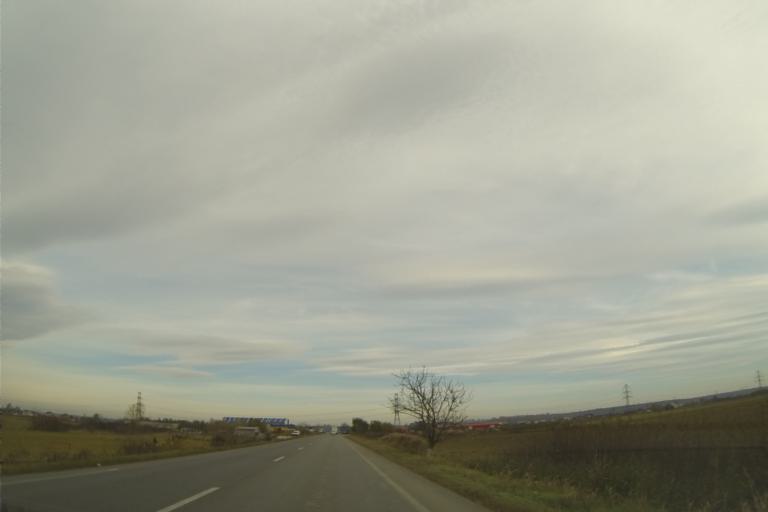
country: RO
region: Olt
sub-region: Comuna Slatioara
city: Slatioara
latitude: 44.4146
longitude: 24.3128
